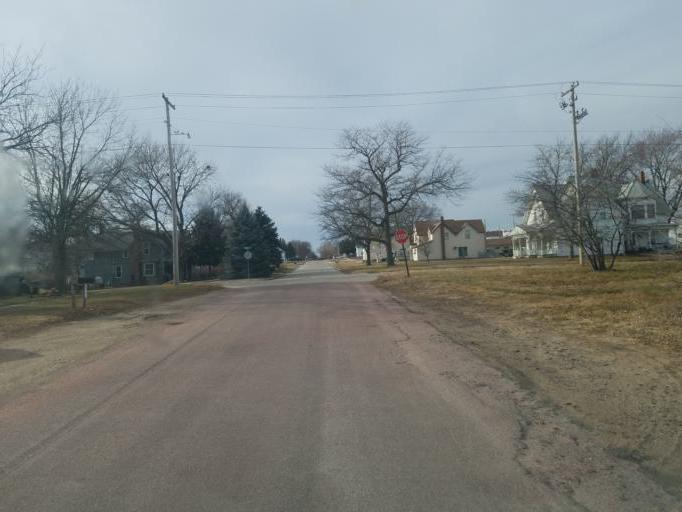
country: US
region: Nebraska
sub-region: Knox County
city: Creighton
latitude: 42.4655
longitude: -97.9030
